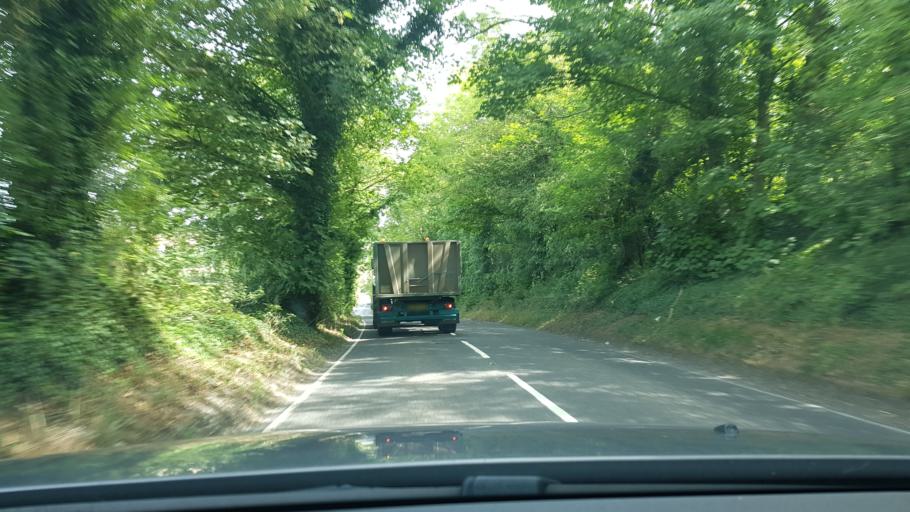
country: GB
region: England
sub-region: West Berkshire
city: Lambourn
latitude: 51.4974
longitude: -1.5422
